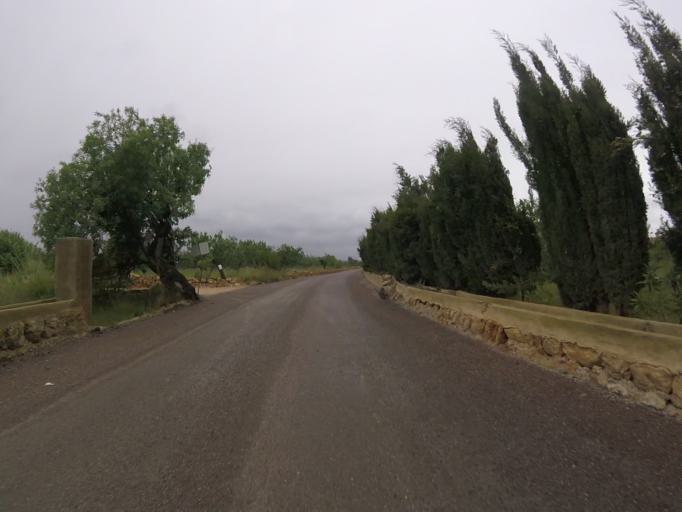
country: ES
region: Valencia
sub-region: Provincia de Castello
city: Alcoceber
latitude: 40.2360
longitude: 0.2550
